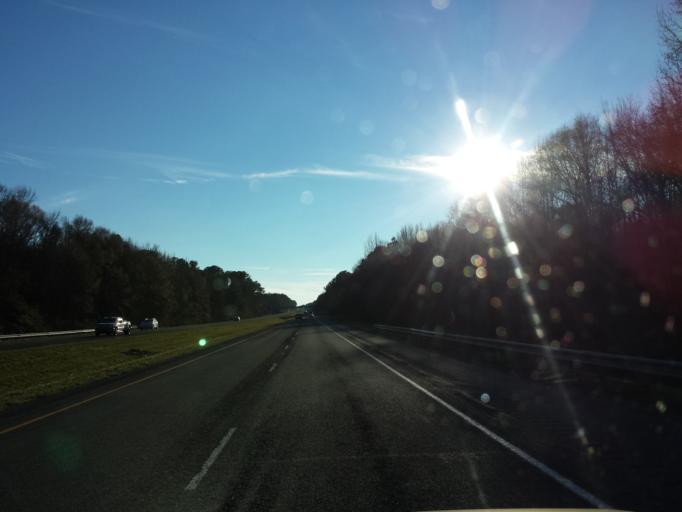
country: US
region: Alabama
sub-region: Greene County
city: Eutaw
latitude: 32.9420
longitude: -87.8494
